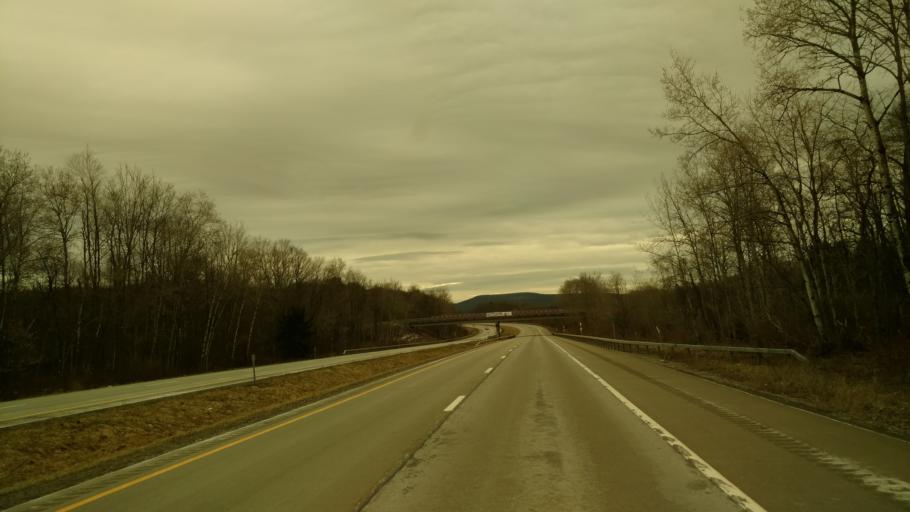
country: US
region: New York
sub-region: Cattaraugus County
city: Salamanca
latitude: 42.1386
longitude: -78.7752
